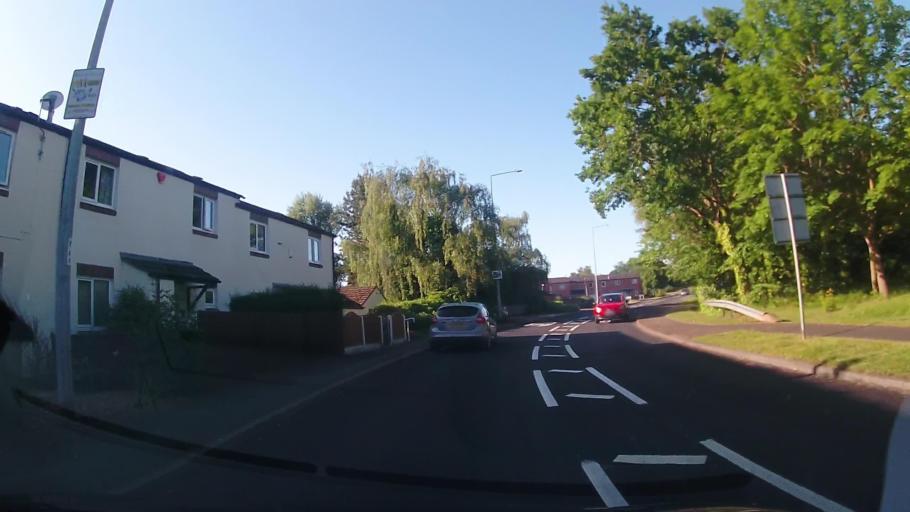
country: GB
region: England
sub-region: Telford and Wrekin
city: Wellington
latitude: 52.7096
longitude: -2.5008
